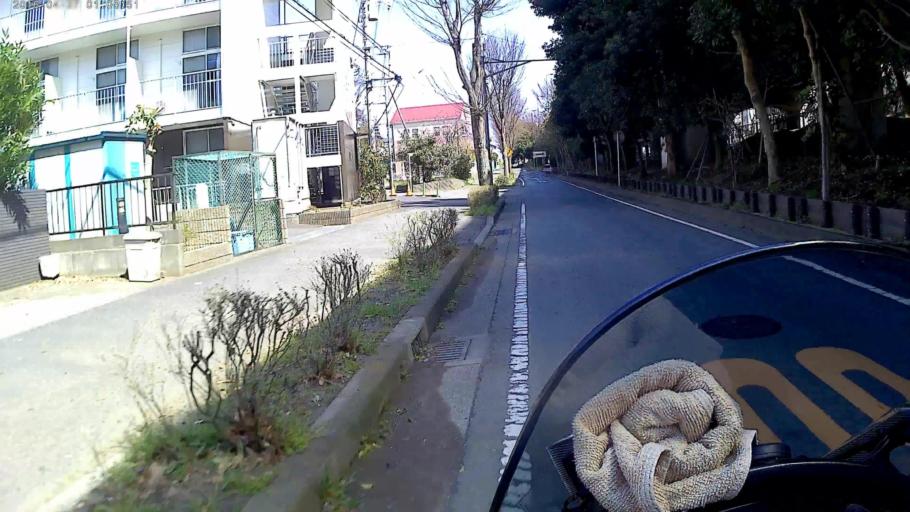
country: JP
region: Kanagawa
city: Fujisawa
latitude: 35.3474
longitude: 139.4448
